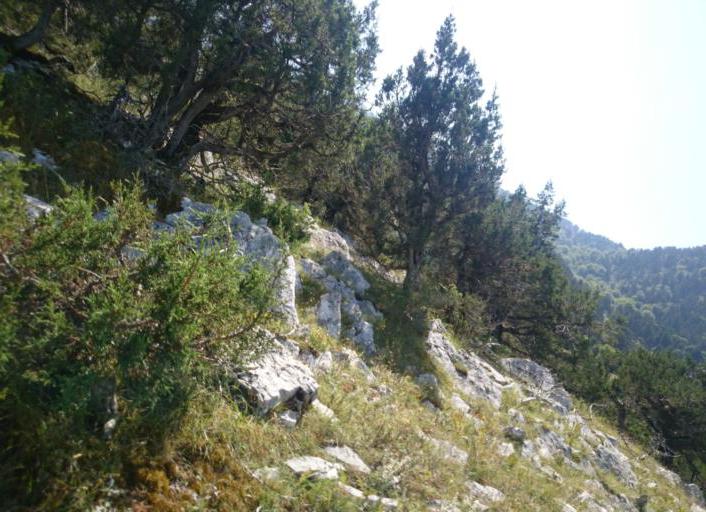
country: AL
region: Elbasan
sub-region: Rrethi i Gramshit
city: Kushove
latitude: 40.7401
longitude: 20.1499
